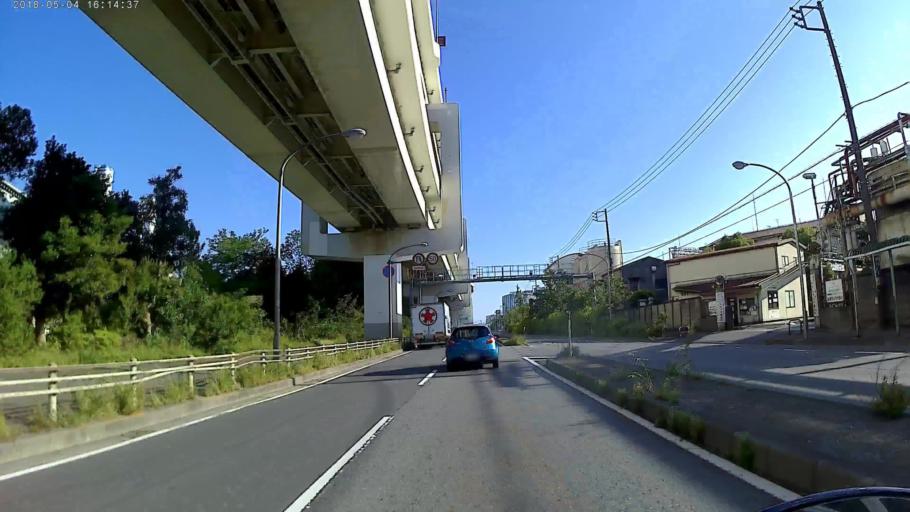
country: JP
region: Kanagawa
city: Yokohama
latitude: 35.4833
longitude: 139.6757
